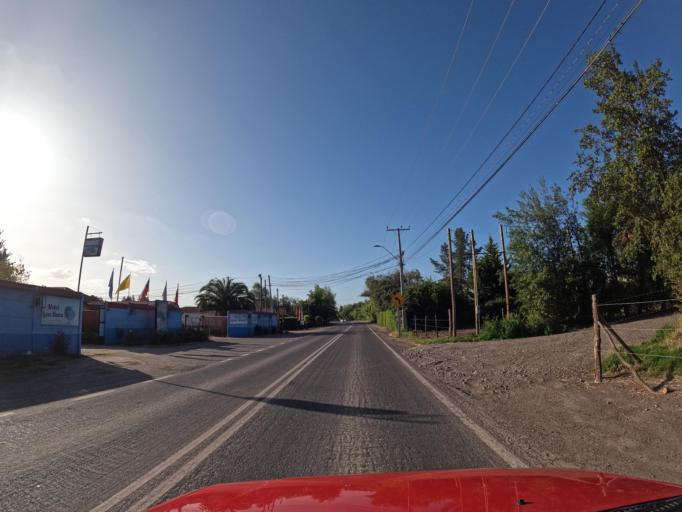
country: CL
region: O'Higgins
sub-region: Provincia de Colchagua
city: Santa Cruz
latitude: -34.6614
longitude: -71.3397
